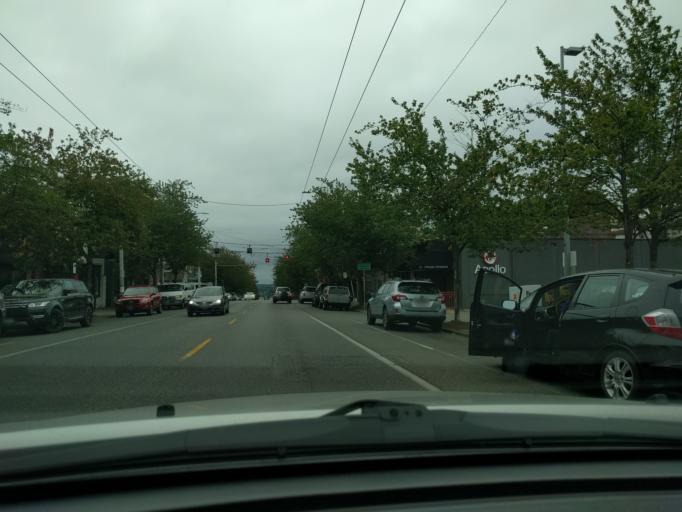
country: US
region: Washington
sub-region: King County
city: Seattle
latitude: 47.6377
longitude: -122.3569
